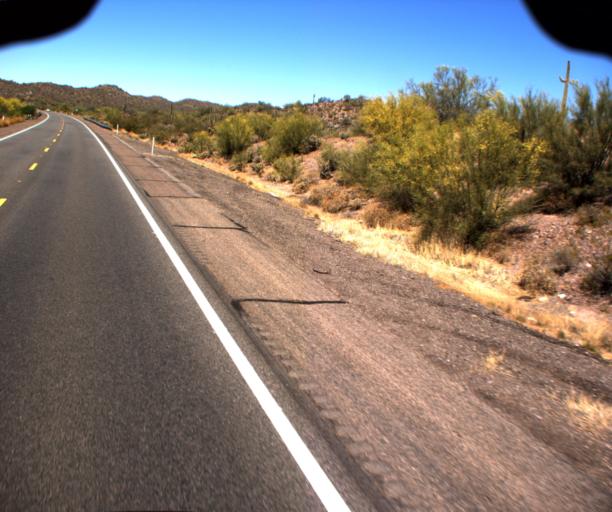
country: US
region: Arizona
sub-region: Maricopa County
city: Sun City West
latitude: 33.8346
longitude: -112.3544
